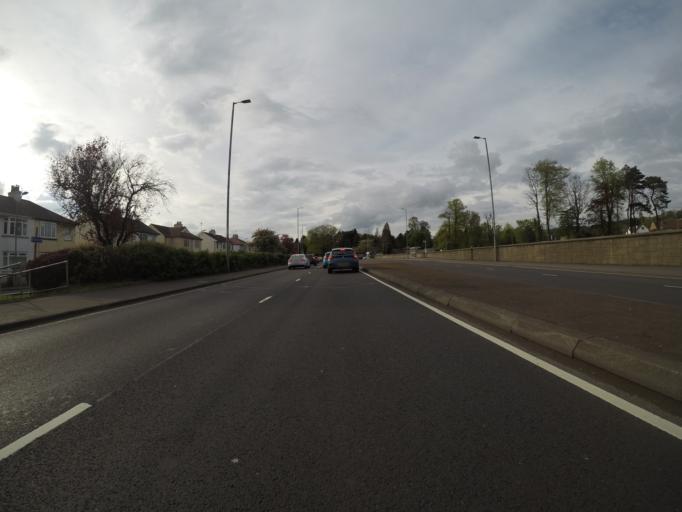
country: GB
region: Scotland
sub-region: West Dunbartonshire
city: Dumbarton
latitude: 55.9485
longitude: -4.5486
